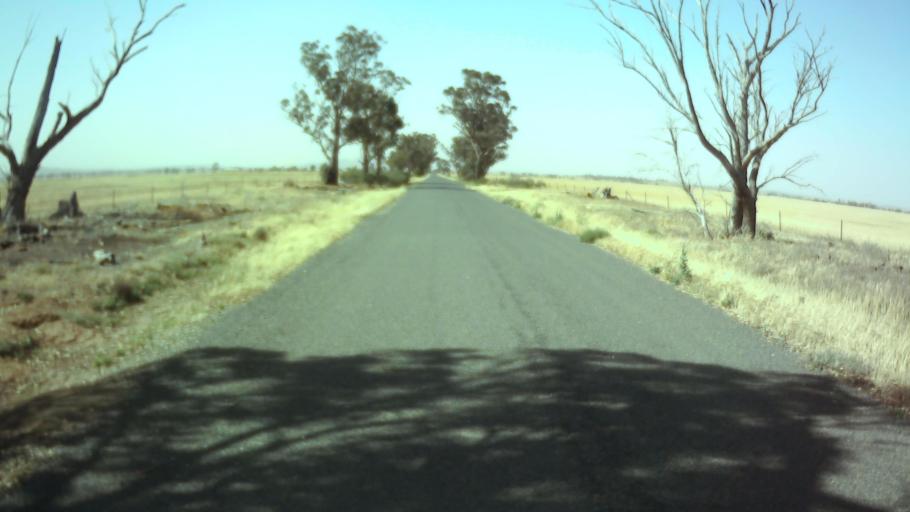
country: AU
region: New South Wales
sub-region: Weddin
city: Grenfell
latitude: -33.8891
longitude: 147.9229
